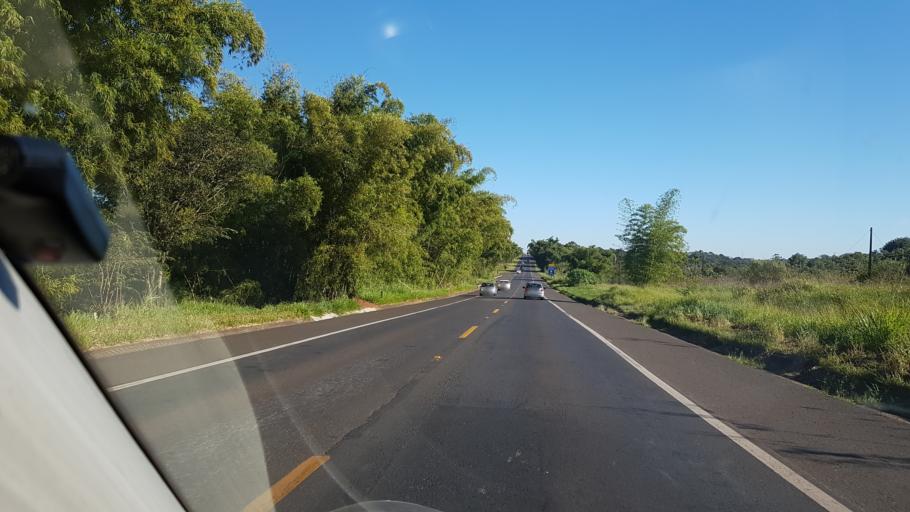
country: BR
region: Sao Paulo
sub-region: Assis
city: Assis
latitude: -22.6284
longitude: -50.4435
